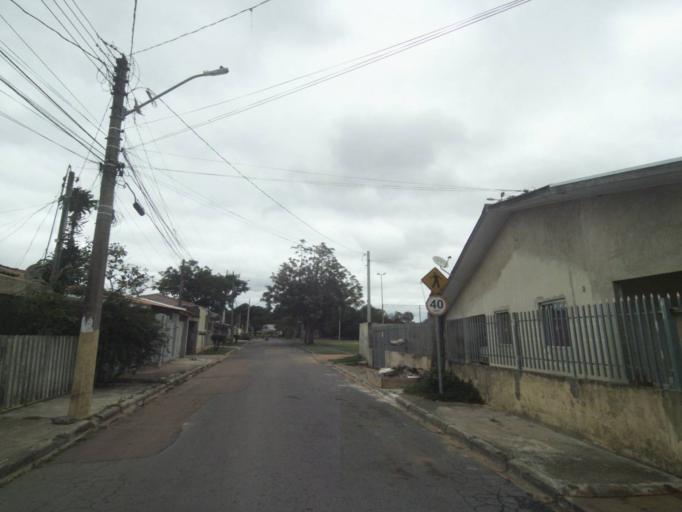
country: BR
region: Parana
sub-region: Sao Jose Dos Pinhais
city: Sao Jose dos Pinhais
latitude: -25.5516
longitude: -49.2564
